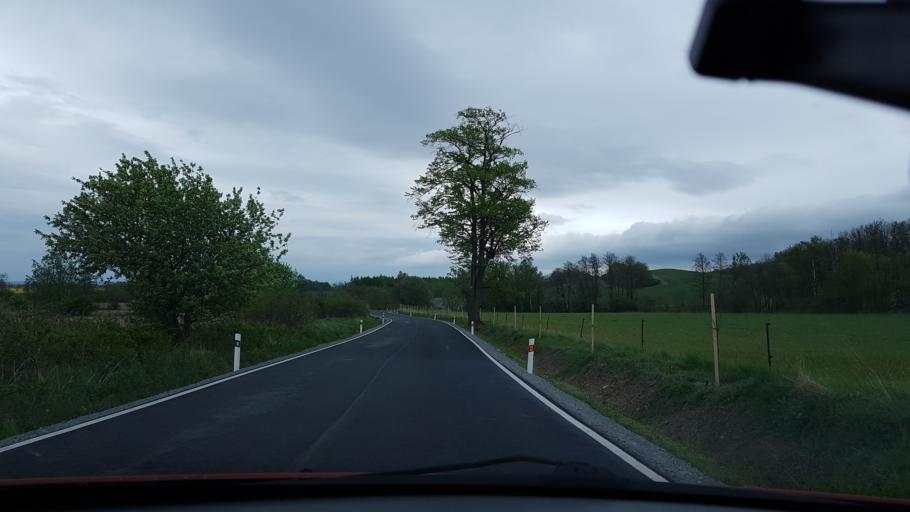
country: PL
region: Opole Voivodeship
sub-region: Powiat nyski
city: Kamienica
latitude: 50.4336
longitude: 16.9467
